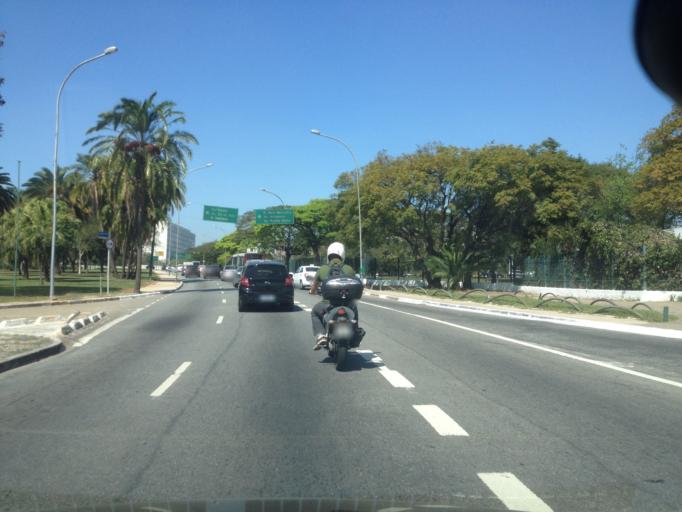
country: BR
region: Sao Paulo
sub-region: Sao Paulo
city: Sao Paulo
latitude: -23.5856
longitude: -46.6553
